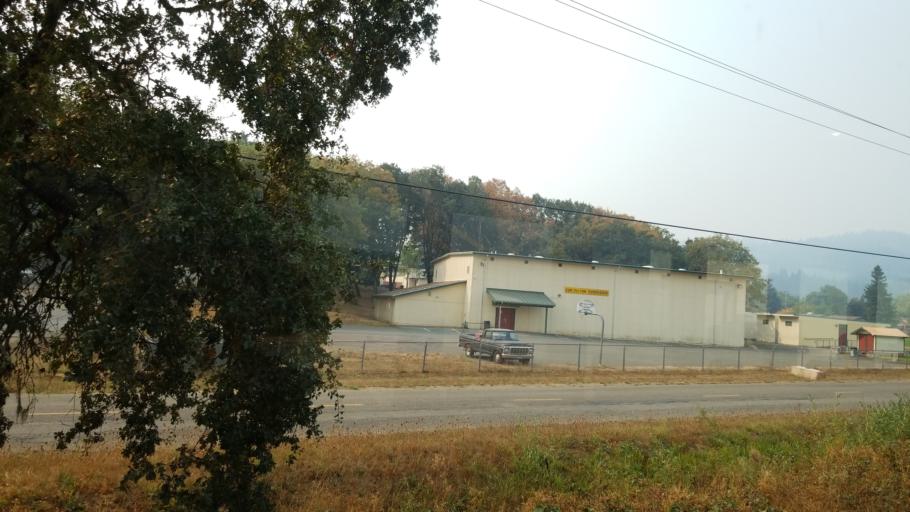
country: US
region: California
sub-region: Mendocino County
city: Willits
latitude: 39.4023
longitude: -123.3525
